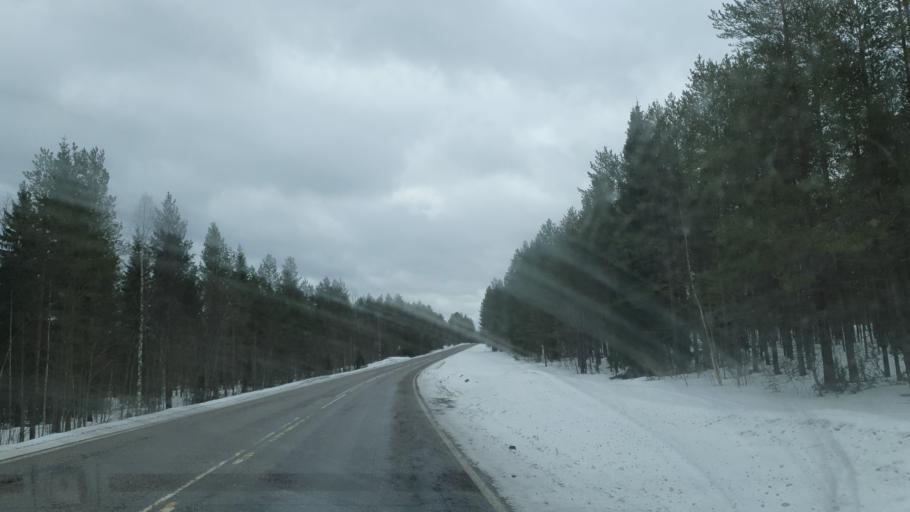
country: FI
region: Northern Ostrobothnia
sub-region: Oulunkaari
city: Pudasjaervi
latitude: 65.3850
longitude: 27.3210
